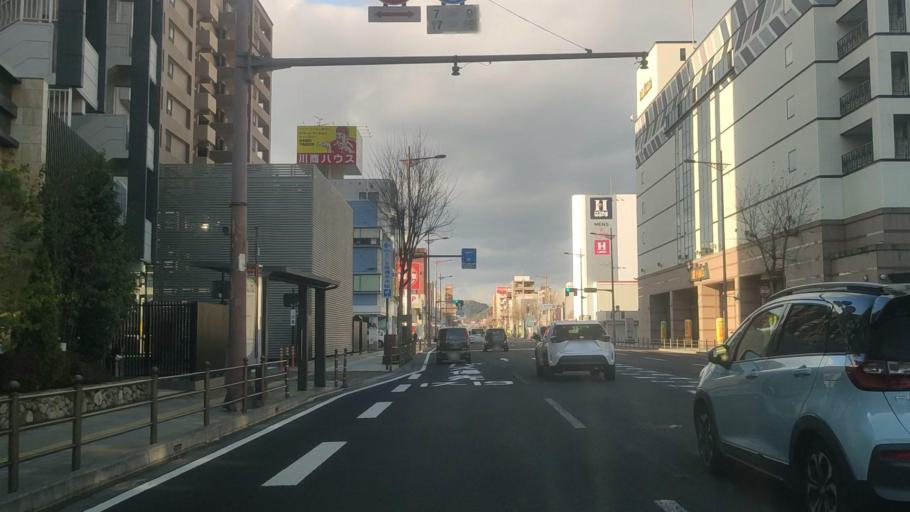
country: JP
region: Kagoshima
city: Kagoshima-shi
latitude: 31.5997
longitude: 130.5398
